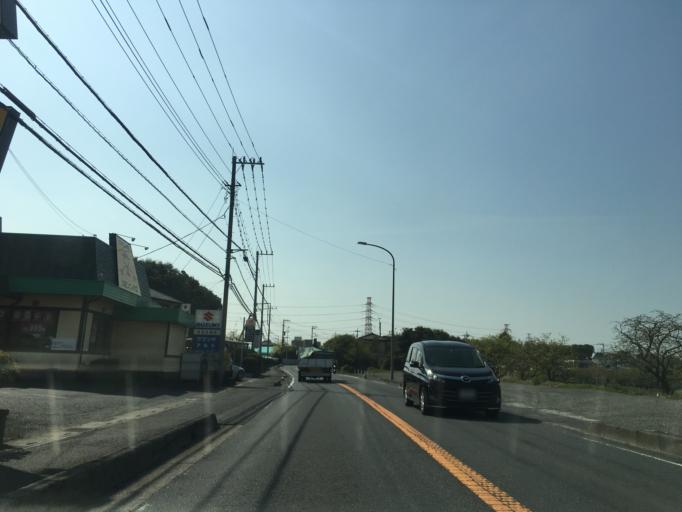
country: JP
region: Saitama
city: Sugito
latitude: 36.0043
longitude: 139.7039
